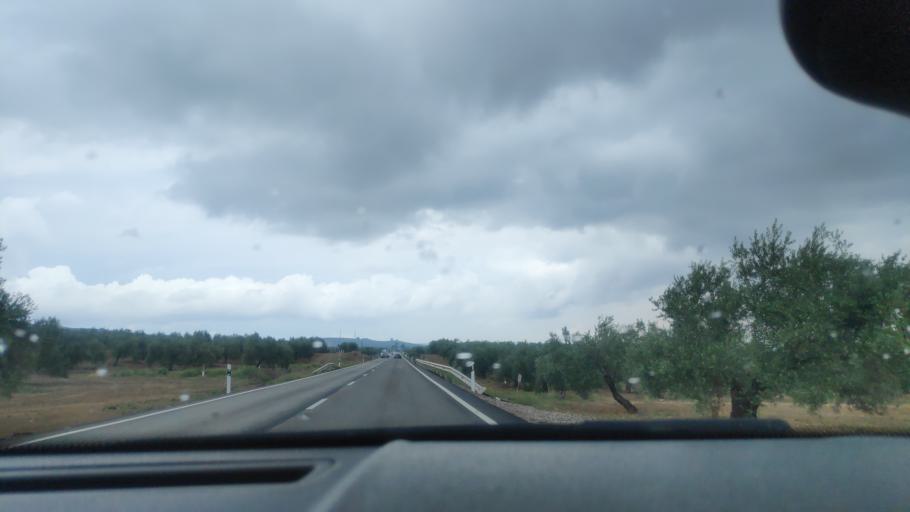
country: ES
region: Andalusia
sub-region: Provincia de Jaen
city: Jabalquinto
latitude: 38.0284
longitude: -3.7689
